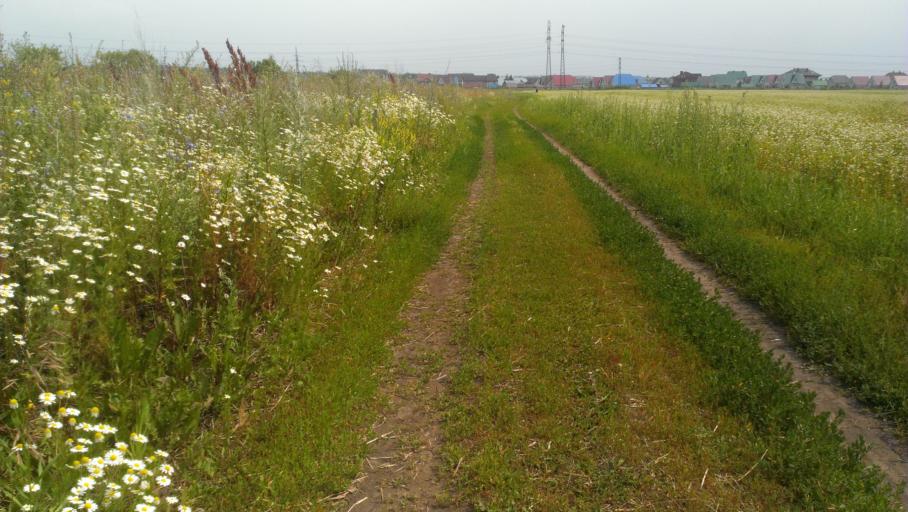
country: RU
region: Altai Krai
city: Novosilikatnyy
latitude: 53.3747
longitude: 83.6463
